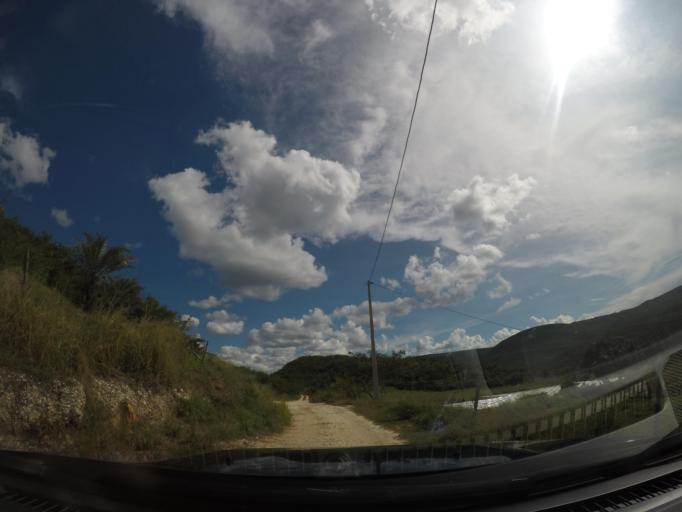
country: BR
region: Bahia
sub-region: Barra Da Estiva
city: Barra da Estiva
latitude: -13.1308
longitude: -41.5950
